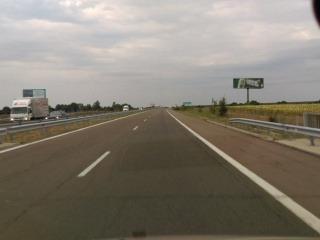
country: BG
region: Burgas
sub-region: Obshtina Karnobat
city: Karnobat
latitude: 42.5902
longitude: 27.0525
